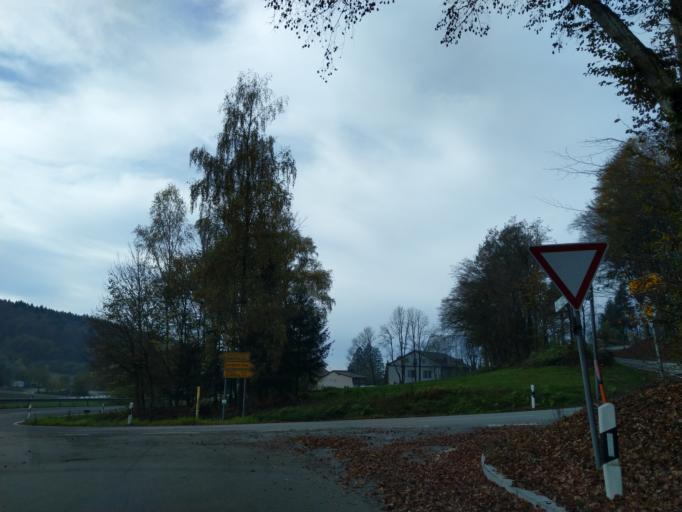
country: DE
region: Bavaria
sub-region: Lower Bavaria
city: Zenting
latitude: 48.7920
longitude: 13.2356
